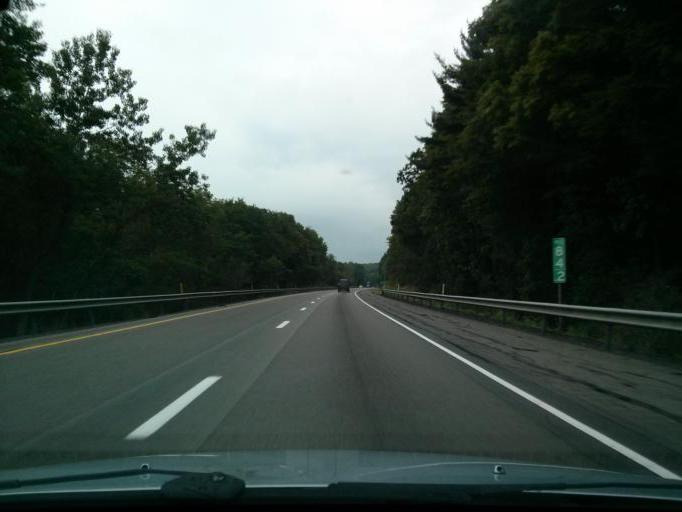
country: US
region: Pennsylvania
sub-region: Jefferson County
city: Brookville
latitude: 41.1575
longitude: -79.0011
